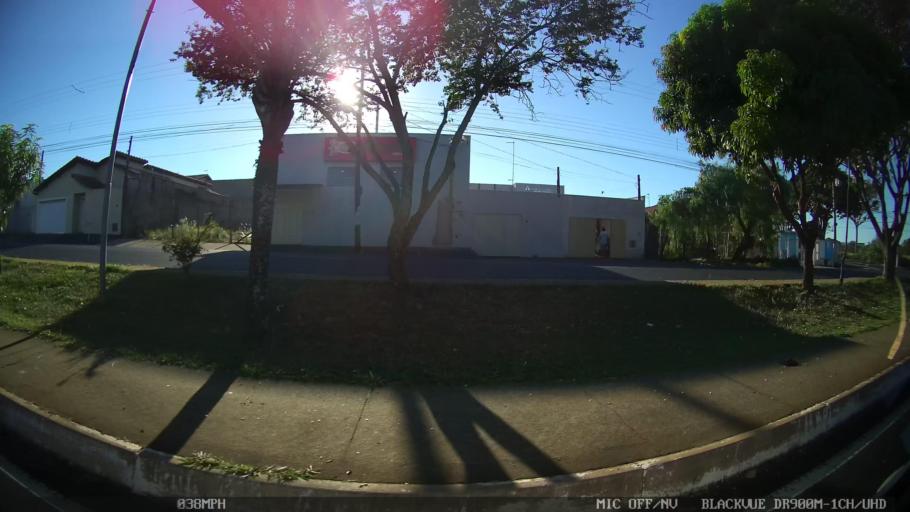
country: BR
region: Sao Paulo
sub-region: Franca
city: Franca
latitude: -20.5830
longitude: -47.3837
